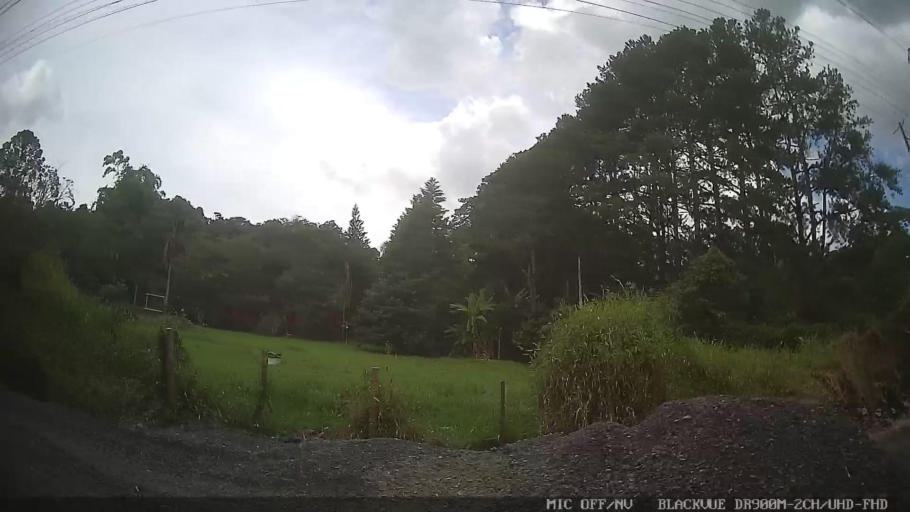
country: BR
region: Minas Gerais
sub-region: Extrema
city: Extrema
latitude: -22.8443
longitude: -46.2515
